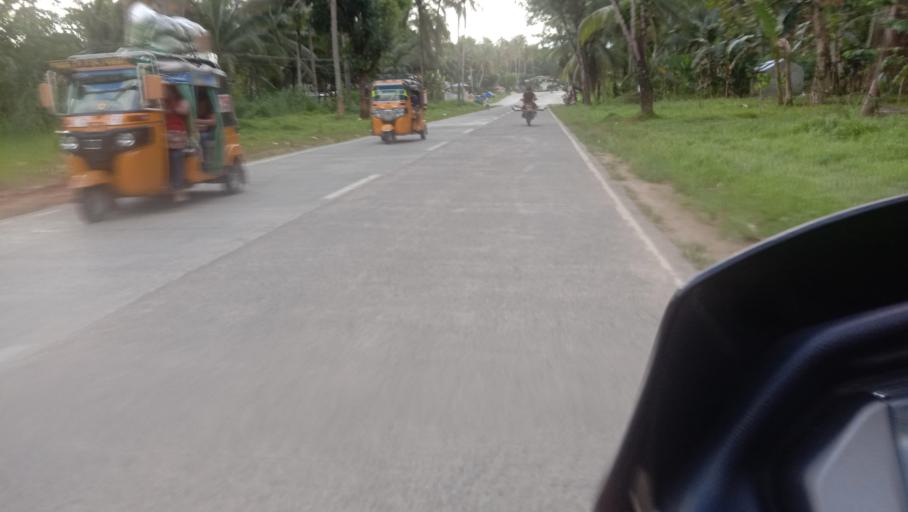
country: PH
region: Caraga
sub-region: Province of Surigao del Sur
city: Barobo
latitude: 8.5169
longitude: 126.1236
